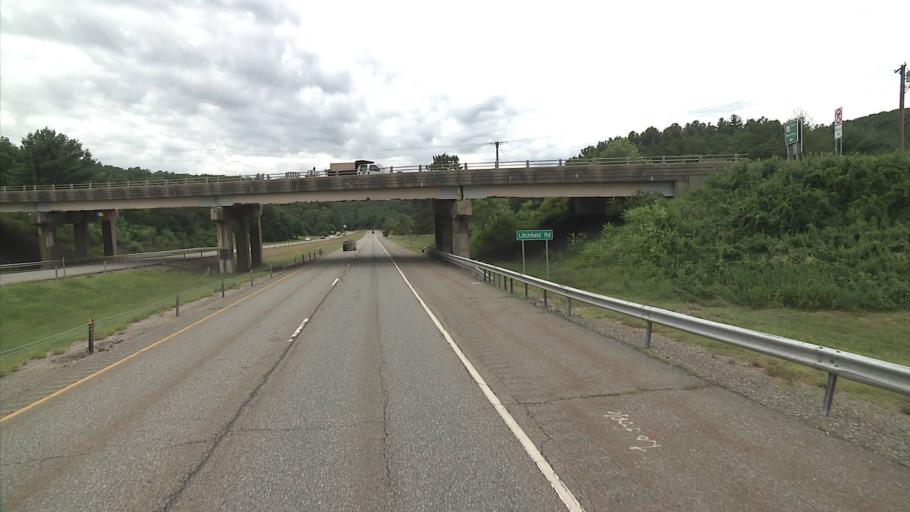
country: US
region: Connecticut
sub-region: Litchfield County
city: Torrington
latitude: 41.7629
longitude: -73.1155
